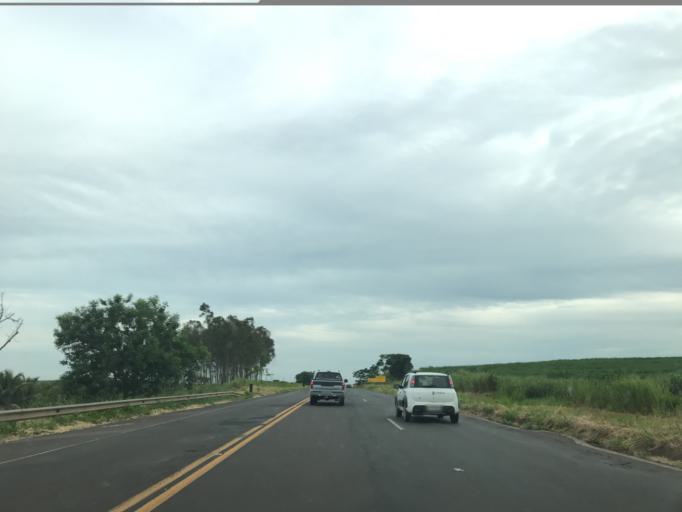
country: BR
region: Sao Paulo
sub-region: Tupa
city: Tupa
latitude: -21.6056
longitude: -50.4716
